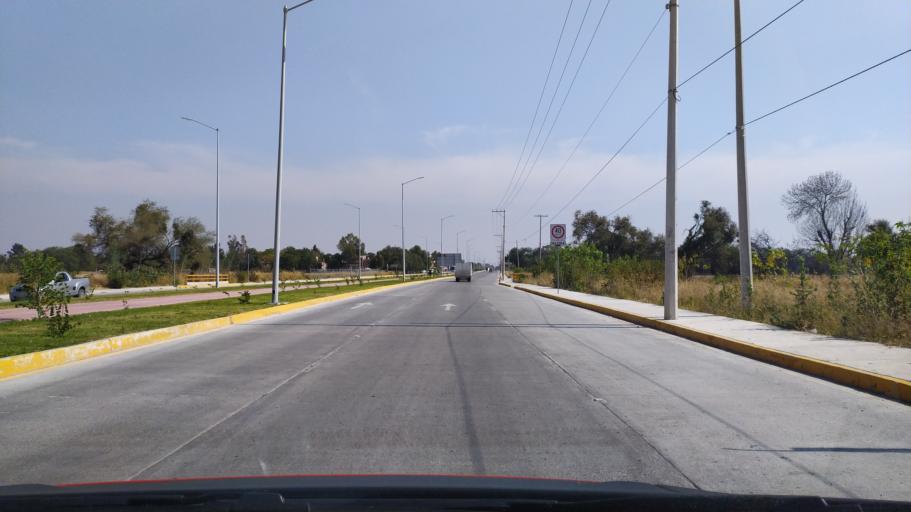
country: MX
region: Guanajuato
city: San Francisco del Rincon
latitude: 21.0249
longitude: -101.8890
